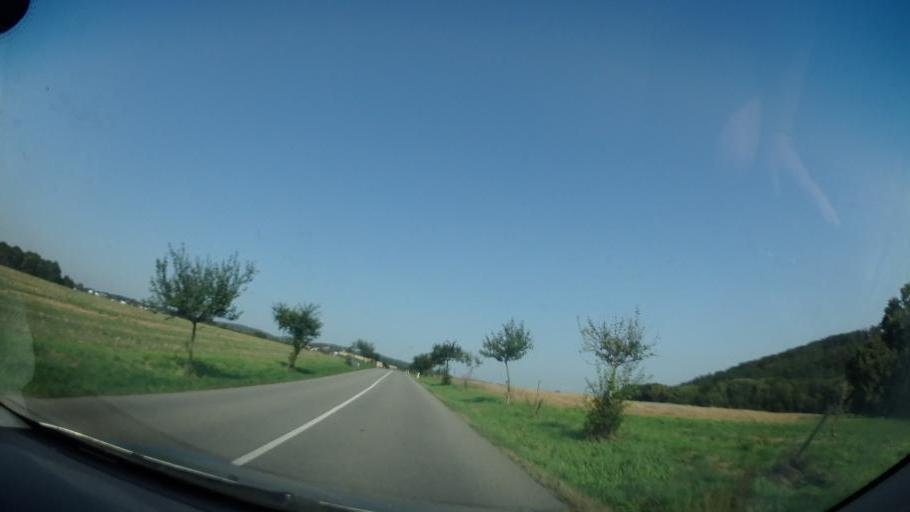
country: CZ
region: South Moravian
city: Kurim
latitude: 49.2464
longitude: 16.5294
